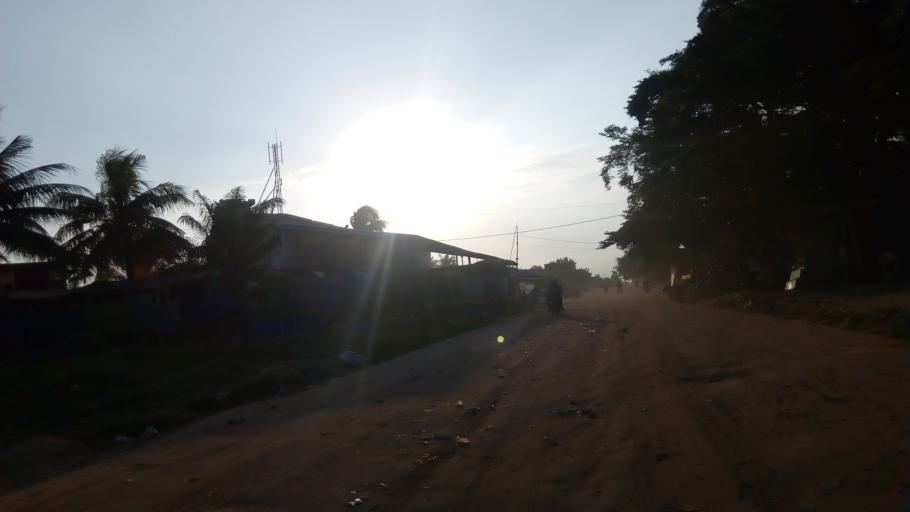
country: TG
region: Maritime
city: Lome
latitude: 6.1821
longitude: 1.1835
